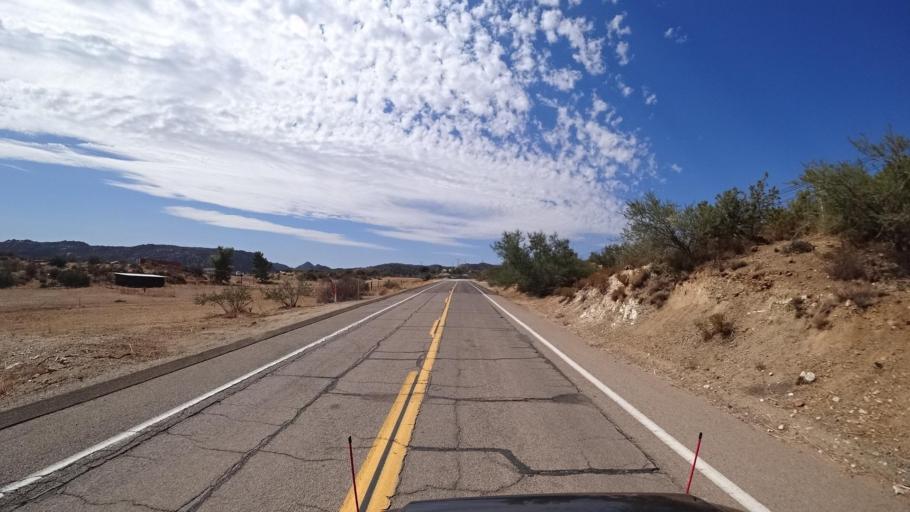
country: MX
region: Baja California
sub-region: Tecate
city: Cereso del Hongo
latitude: 32.6132
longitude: -116.2070
